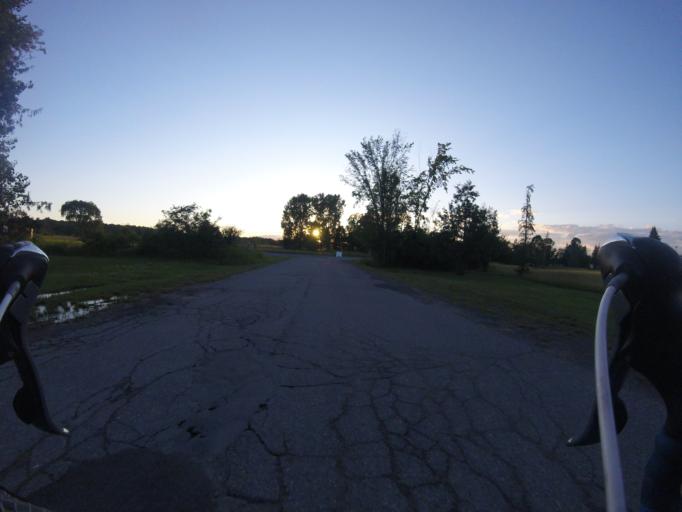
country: CA
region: Ontario
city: Bells Corners
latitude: 45.3371
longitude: -75.8533
